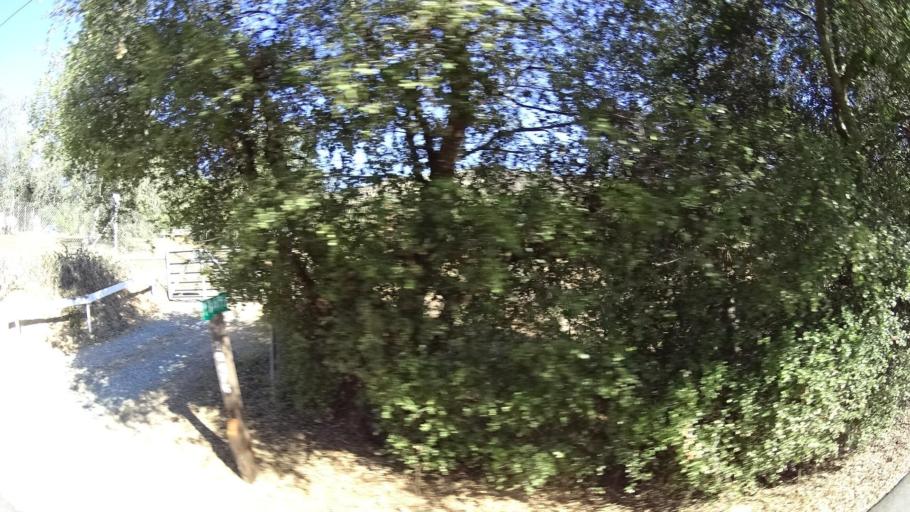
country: US
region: California
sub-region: San Diego County
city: Jamul
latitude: 32.6780
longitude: -116.7301
